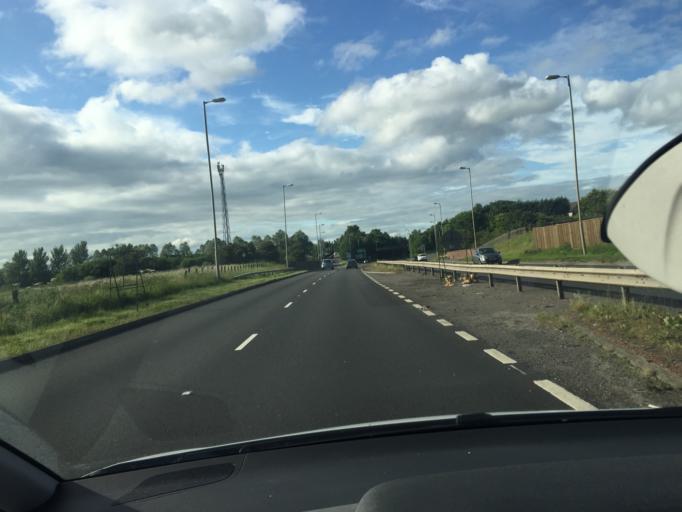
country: GB
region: Scotland
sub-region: North Lanarkshire
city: Bellshill
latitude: 55.8169
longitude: -4.0394
